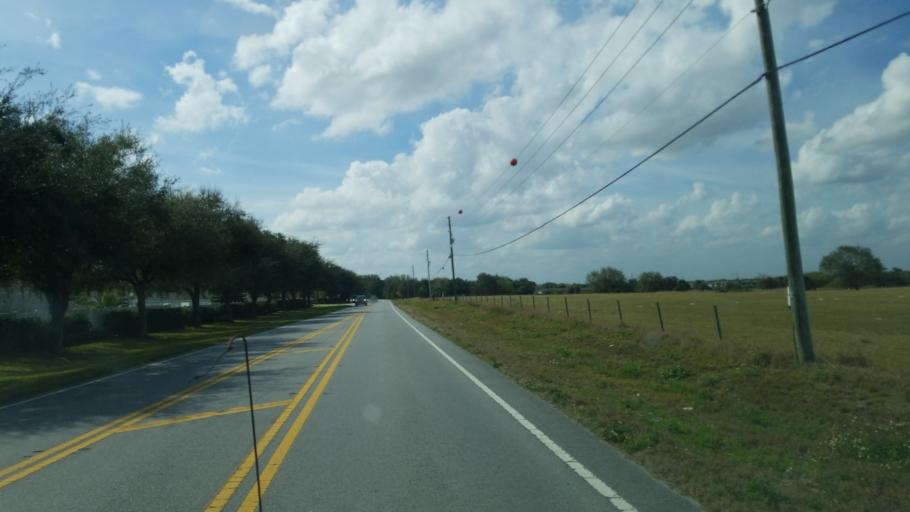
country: US
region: Florida
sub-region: Polk County
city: Lake Wales
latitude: 27.9607
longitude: -81.6013
